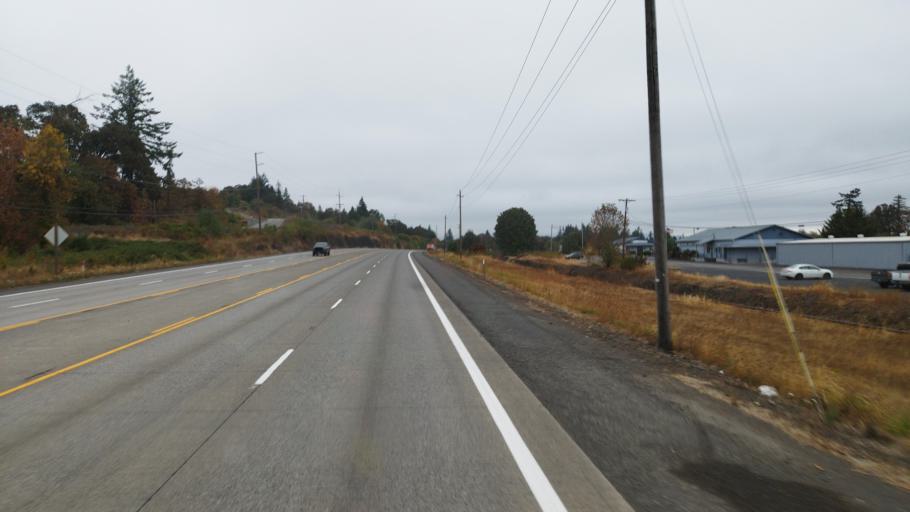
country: US
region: Oregon
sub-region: Columbia County
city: Saint Helens
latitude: 45.8718
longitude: -122.8146
